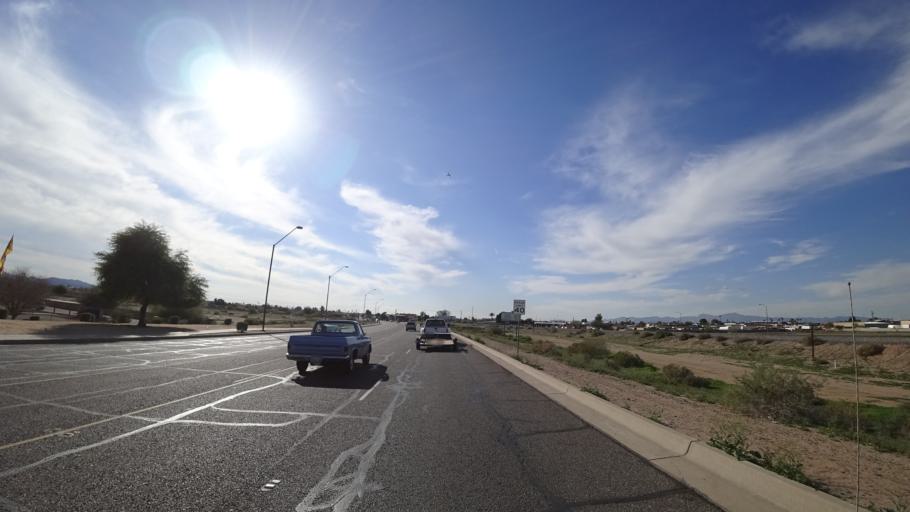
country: US
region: Arizona
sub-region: Maricopa County
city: Avondale
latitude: 33.4350
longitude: -112.3369
